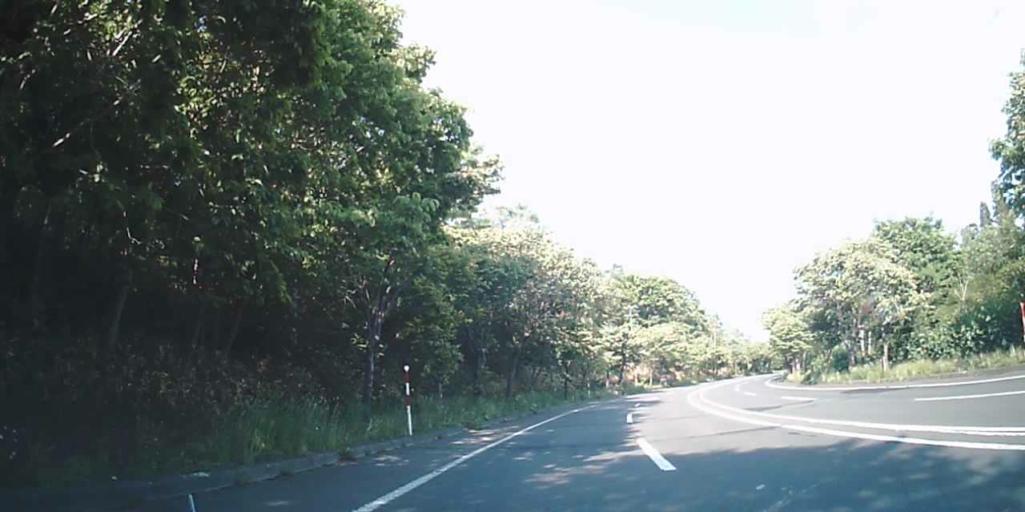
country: JP
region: Hokkaido
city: Shiraoi
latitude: 42.4656
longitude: 141.1743
